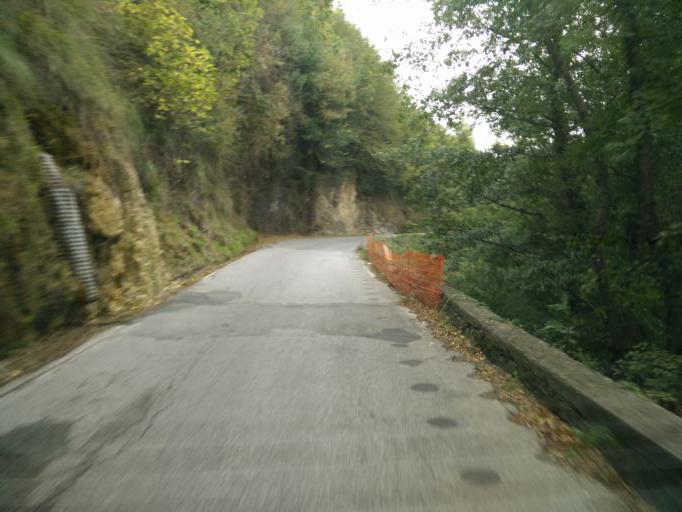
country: IT
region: Tuscany
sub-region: Provincia di Massa-Carrara
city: Casola in Lunigiana
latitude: 44.1904
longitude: 10.1440
